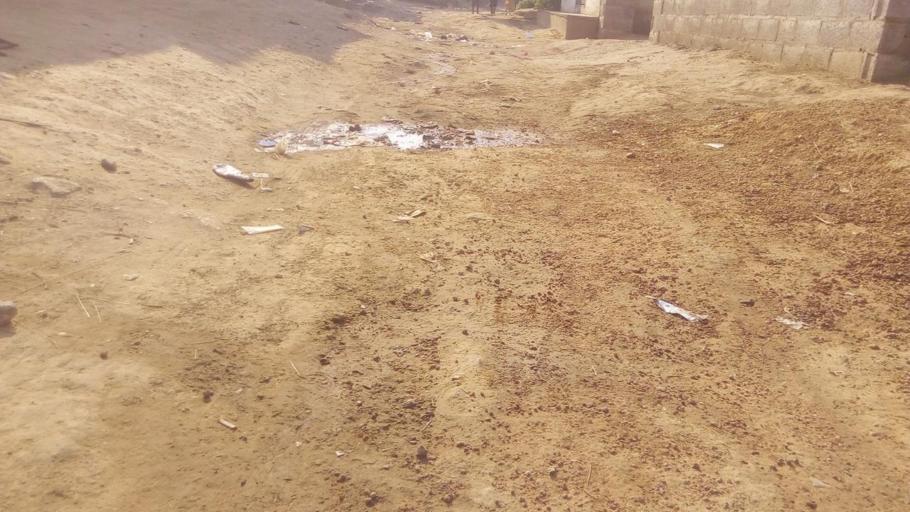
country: ZM
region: Lusaka
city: Lusaka
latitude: -15.3598
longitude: 28.2881
